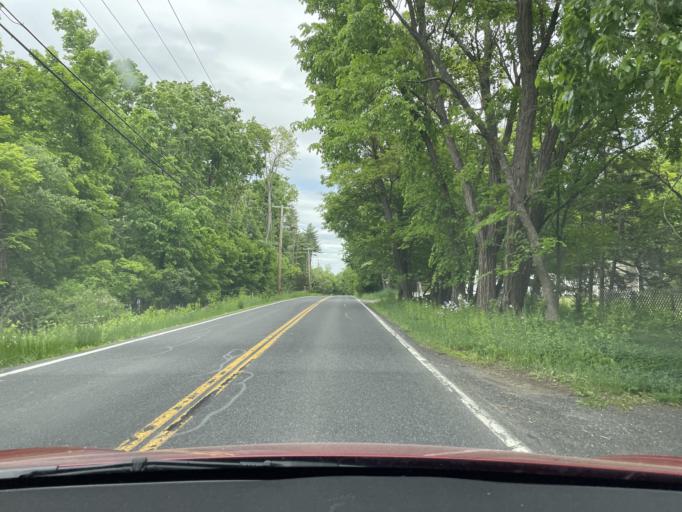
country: US
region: New York
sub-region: Ulster County
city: West Hurley
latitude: 42.0144
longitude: -74.1153
